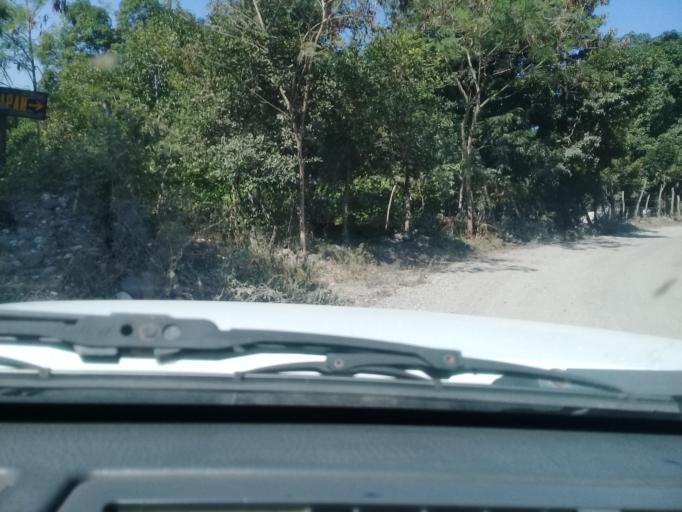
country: MX
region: Veracruz
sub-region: Emiliano Zapata
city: Plan del Rio
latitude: 19.4269
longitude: -96.6163
